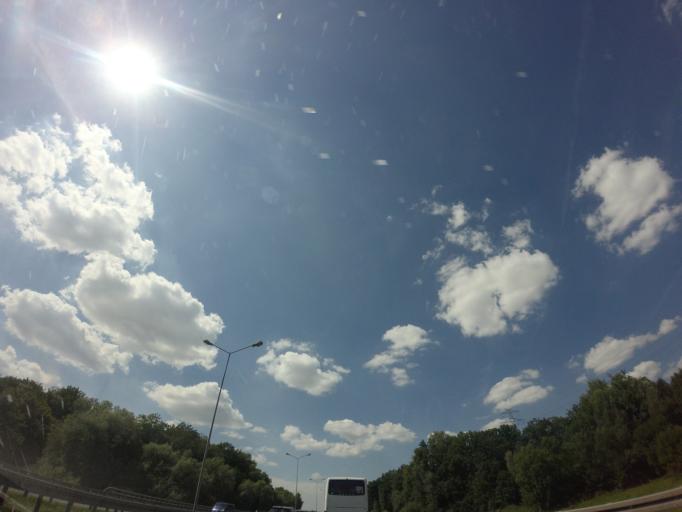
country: PL
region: Lower Silesian Voivodeship
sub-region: Powiat strzelinski
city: Wiazow
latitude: 50.8477
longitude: 17.2455
